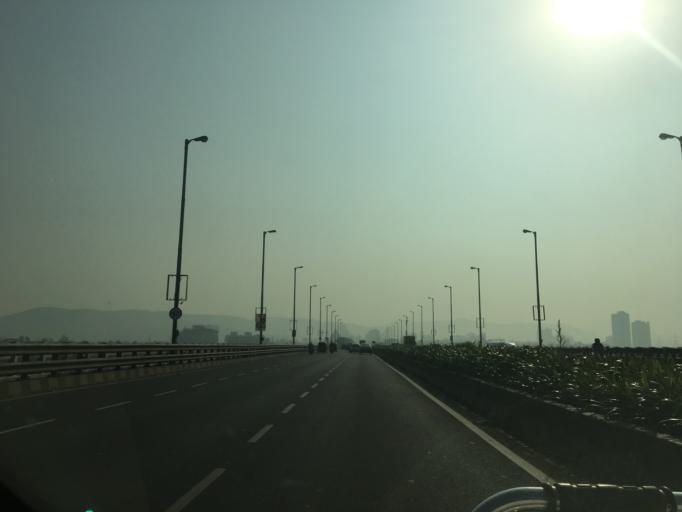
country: IN
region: Maharashtra
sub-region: Thane
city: Airoli
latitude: 19.1511
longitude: 72.9786
